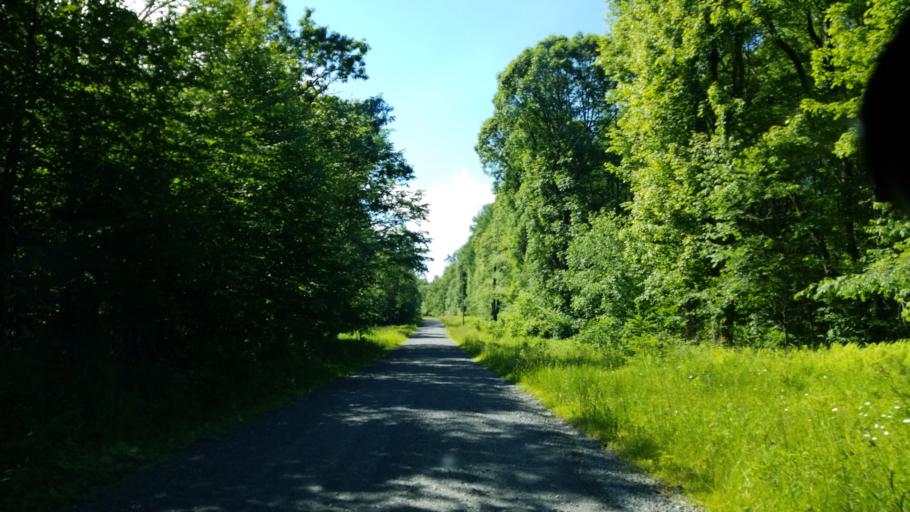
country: US
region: Pennsylvania
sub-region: Clearfield County
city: Clearfield
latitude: 41.1869
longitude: -78.4630
